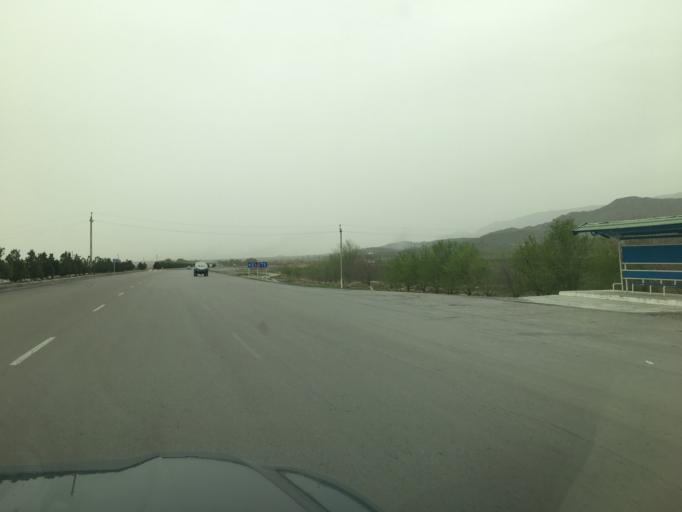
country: TM
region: Ahal
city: Baharly
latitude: 38.2684
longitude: 57.7092
